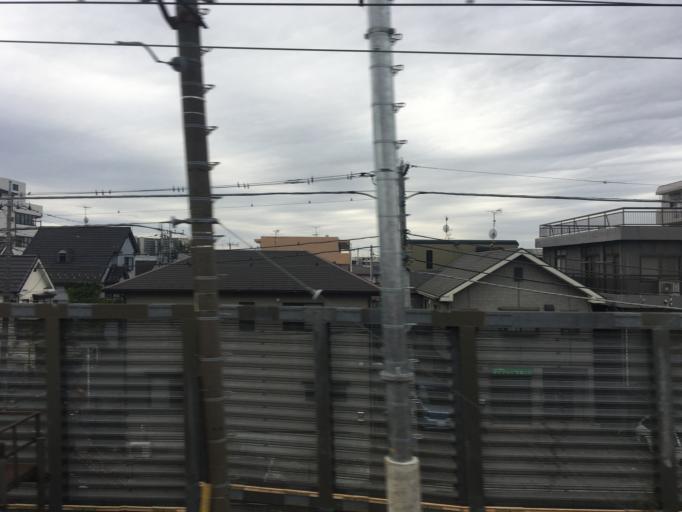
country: JP
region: Chiba
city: Nagareyama
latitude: 35.8404
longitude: 139.9017
